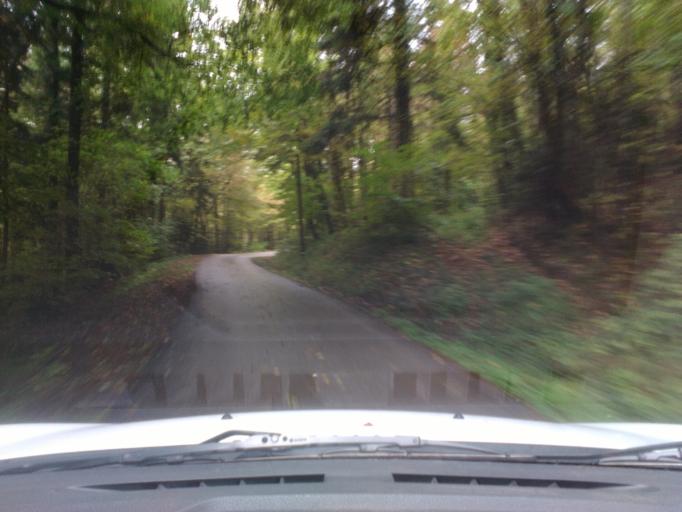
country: FR
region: Lorraine
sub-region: Departement des Vosges
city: Saint-Die-des-Vosges
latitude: 48.3091
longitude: 6.9761
